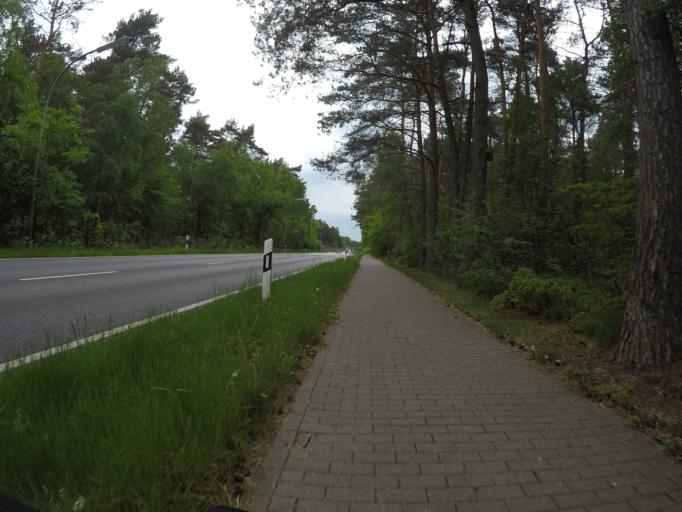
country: DE
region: Schleswig-Holstein
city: Norderstedt
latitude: 53.7154
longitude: 9.9801
